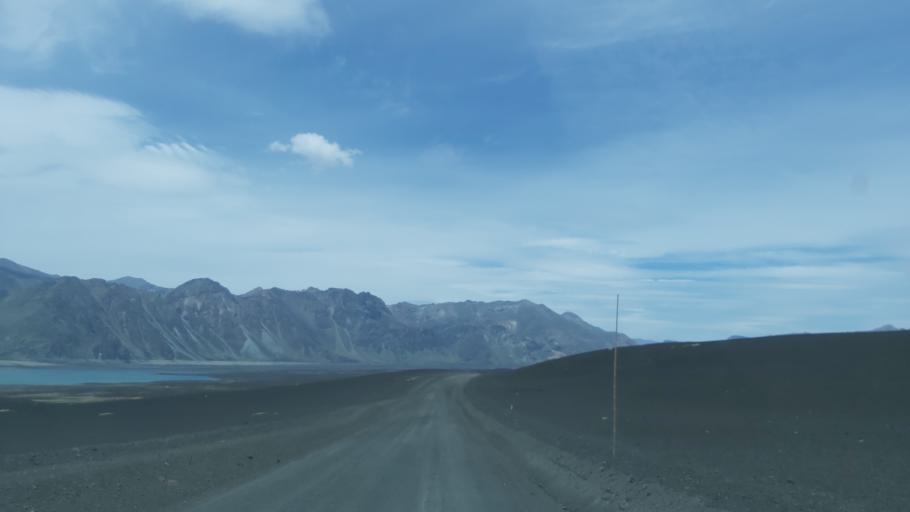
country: AR
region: Neuquen
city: Andacollo
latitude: -37.4147
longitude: -71.2908
